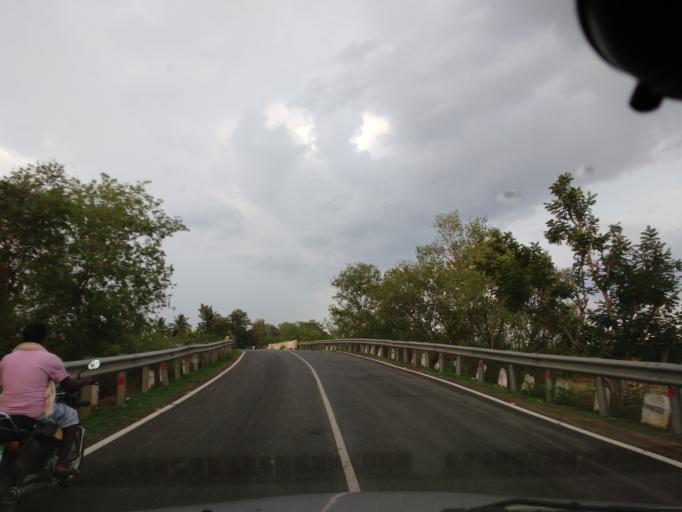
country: IN
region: Karnataka
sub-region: Tumkur
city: Tiptur
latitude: 13.2670
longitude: 76.4331
